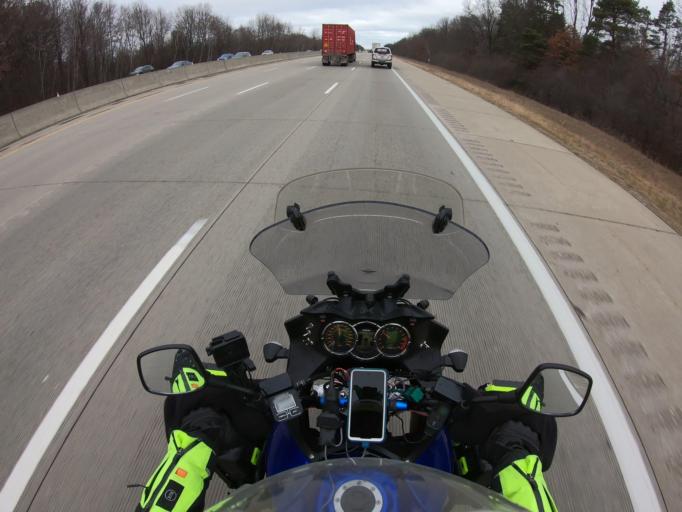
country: US
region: Michigan
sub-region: Saginaw County
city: Bridgeport
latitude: 43.3113
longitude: -83.8367
